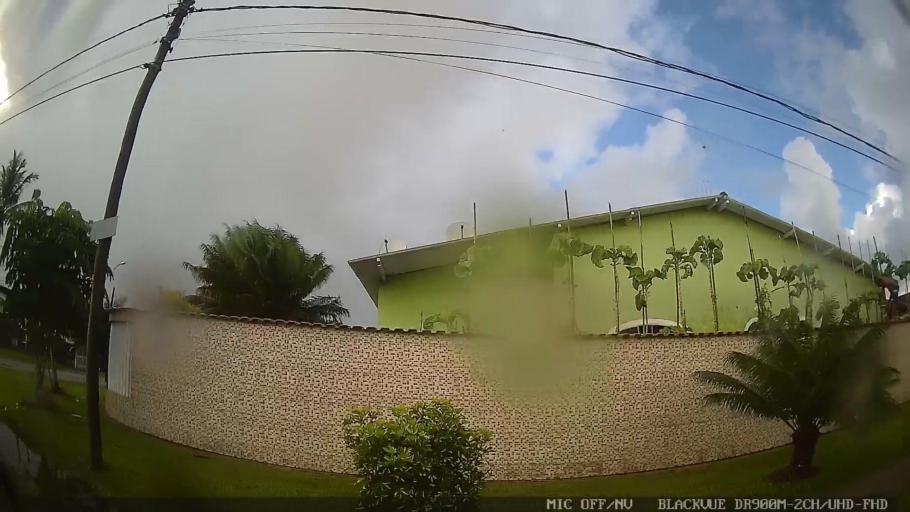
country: BR
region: Sao Paulo
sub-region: Itanhaem
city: Itanhaem
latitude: -24.2405
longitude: -46.9006
